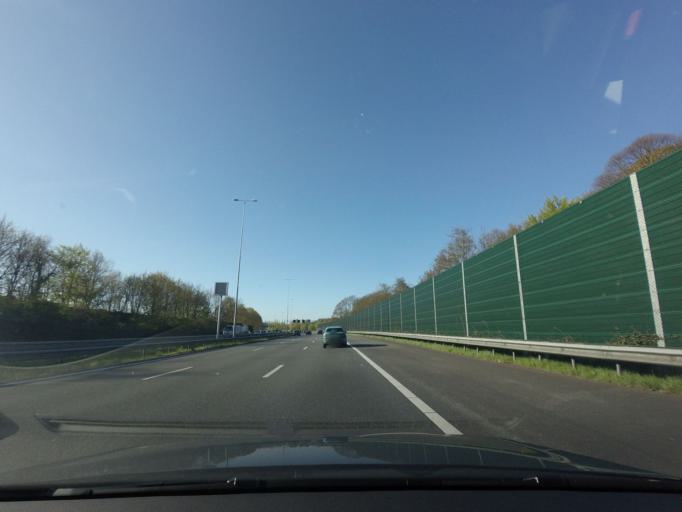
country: NL
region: North Holland
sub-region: Gemeente Naarden
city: Naarden
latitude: 52.2864
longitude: 5.1839
